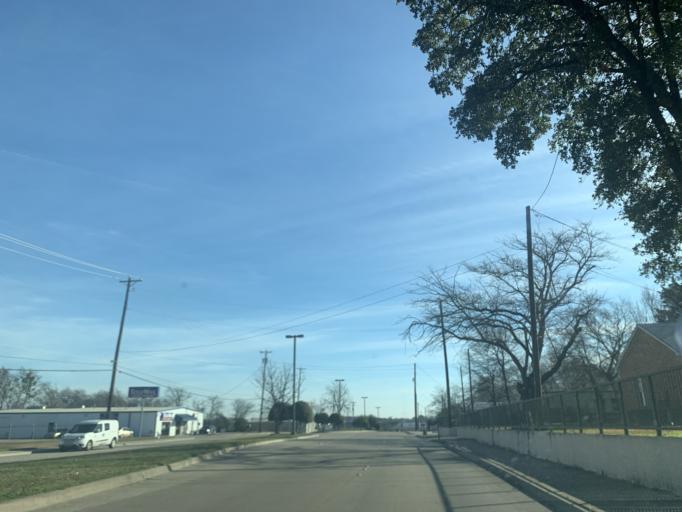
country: US
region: Texas
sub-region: Dallas County
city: DeSoto
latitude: 32.5751
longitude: -96.8262
